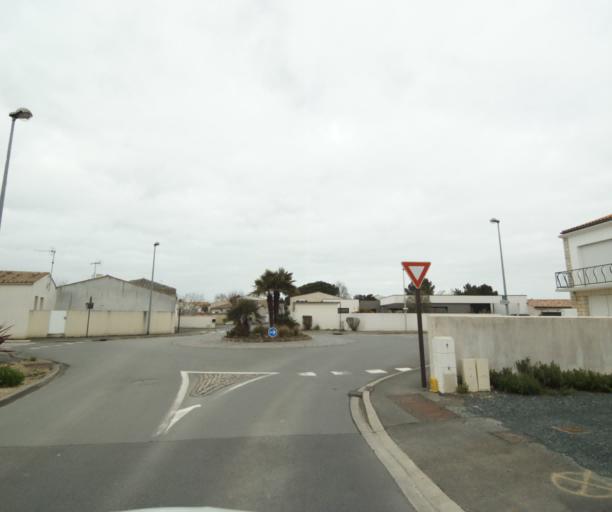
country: FR
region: Poitou-Charentes
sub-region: Departement de la Charente-Maritime
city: Lagord
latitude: 46.1916
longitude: -1.1511
